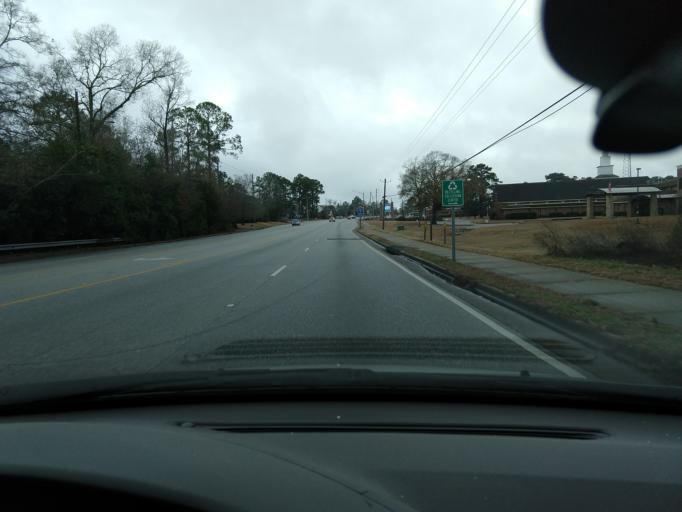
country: US
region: Alabama
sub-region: Houston County
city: Dothan
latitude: 31.2413
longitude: -85.4354
